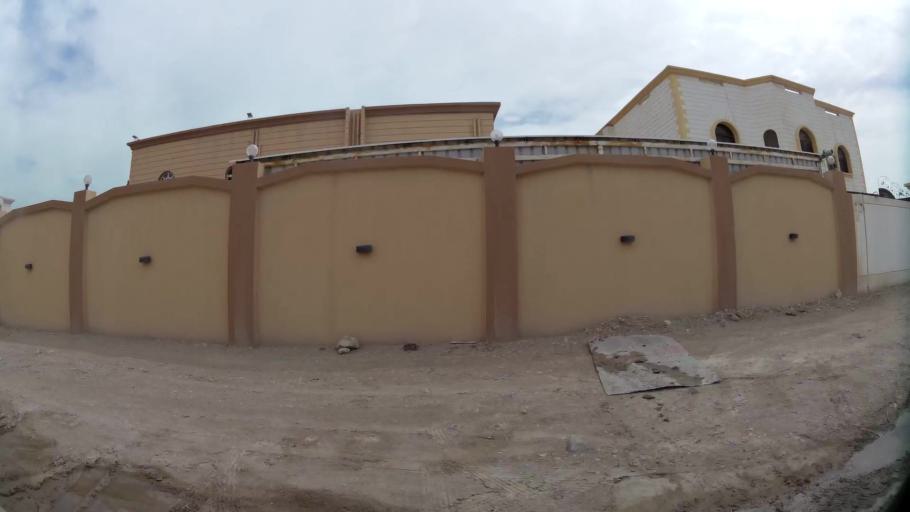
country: QA
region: Baladiyat ar Rayyan
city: Ar Rayyan
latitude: 25.2062
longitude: 51.4529
